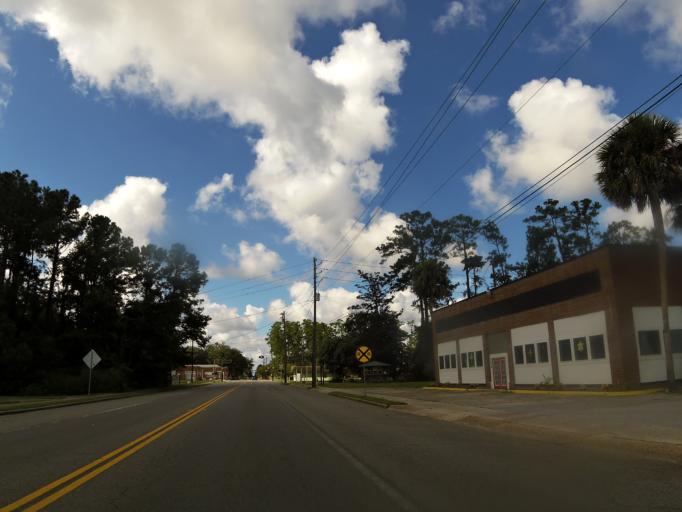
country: US
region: Georgia
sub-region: Camden County
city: Kingsland
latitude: 30.7954
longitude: -81.6893
